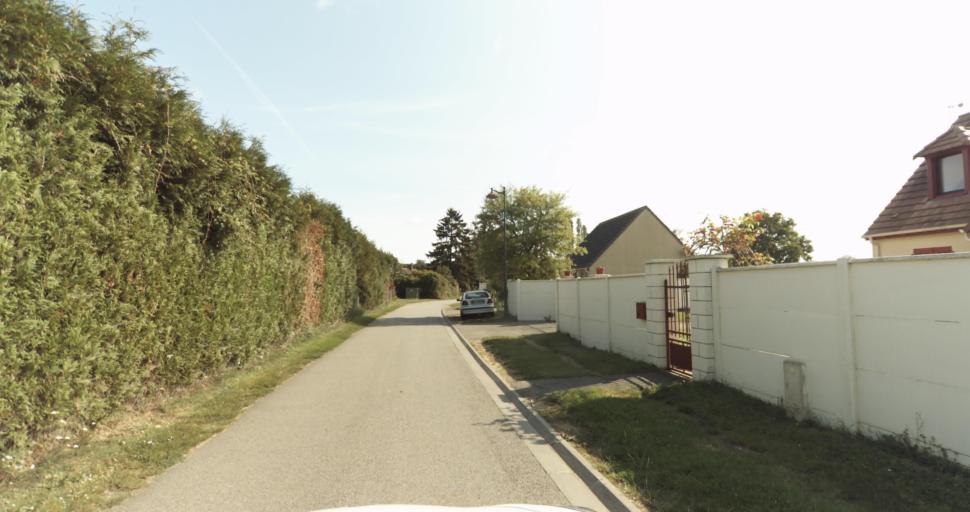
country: FR
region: Haute-Normandie
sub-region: Departement de l'Eure
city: Tillieres-sur-Avre
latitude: 48.7720
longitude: 1.0826
